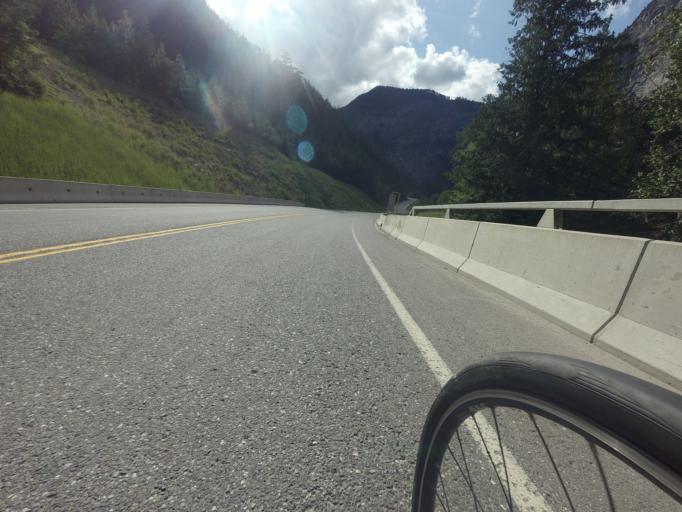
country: CA
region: British Columbia
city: Lillooet
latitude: 50.6441
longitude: -122.0542
